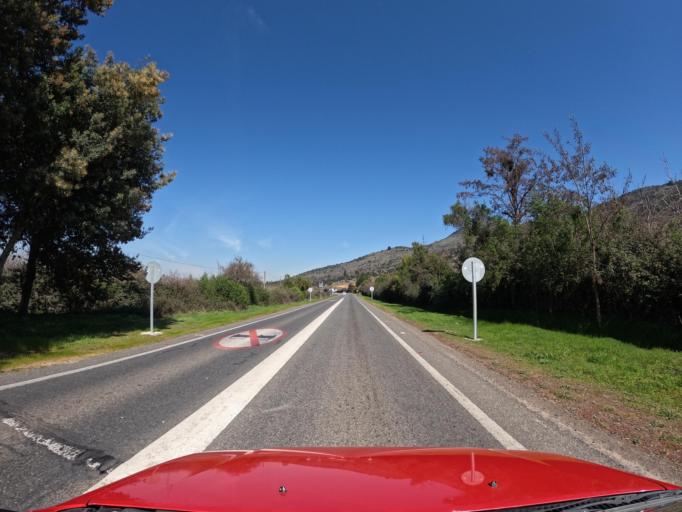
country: CL
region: Maule
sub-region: Provincia de Curico
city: Rauco
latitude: -35.0629
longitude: -71.6203
